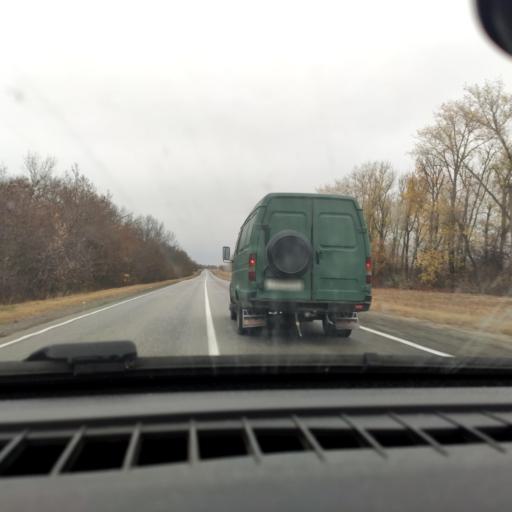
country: RU
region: Voronezj
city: Uryv-Pokrovka
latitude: 51.0878
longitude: 39.0051
